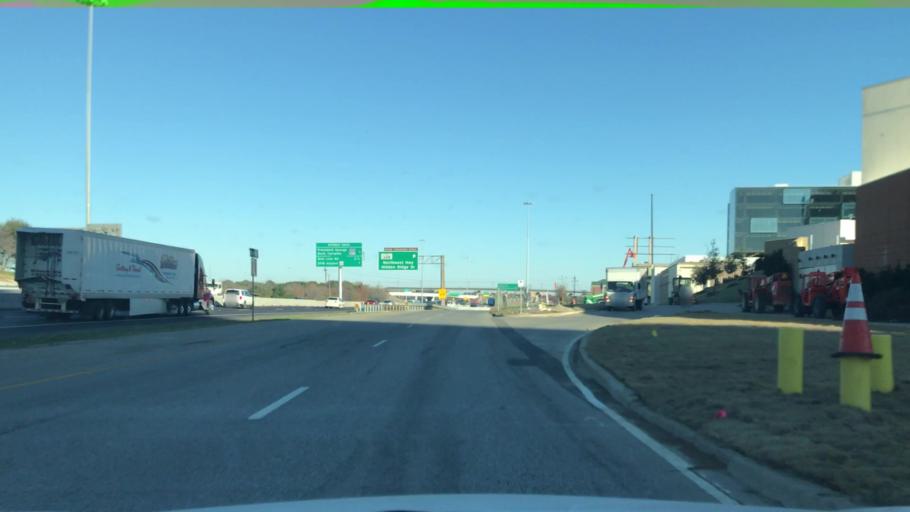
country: US
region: Texas
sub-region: Dallas County
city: Irving
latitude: 32.8728
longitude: -96.9458
